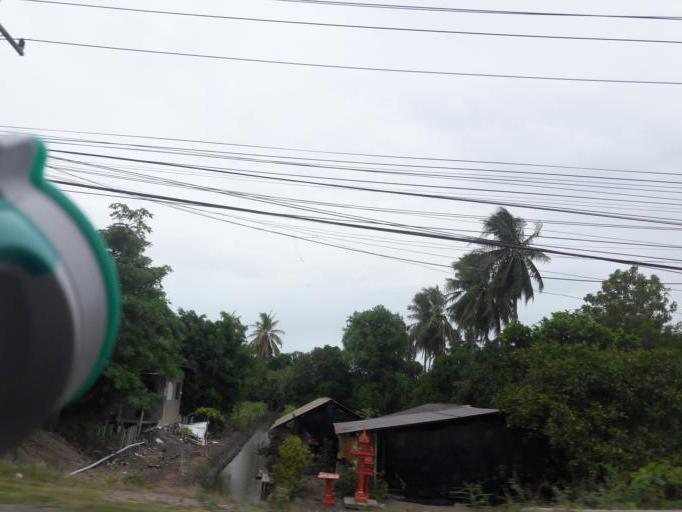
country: TH
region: Ratchaburi
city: Damnoen Saduak
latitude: 13.5471
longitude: 99.9664
